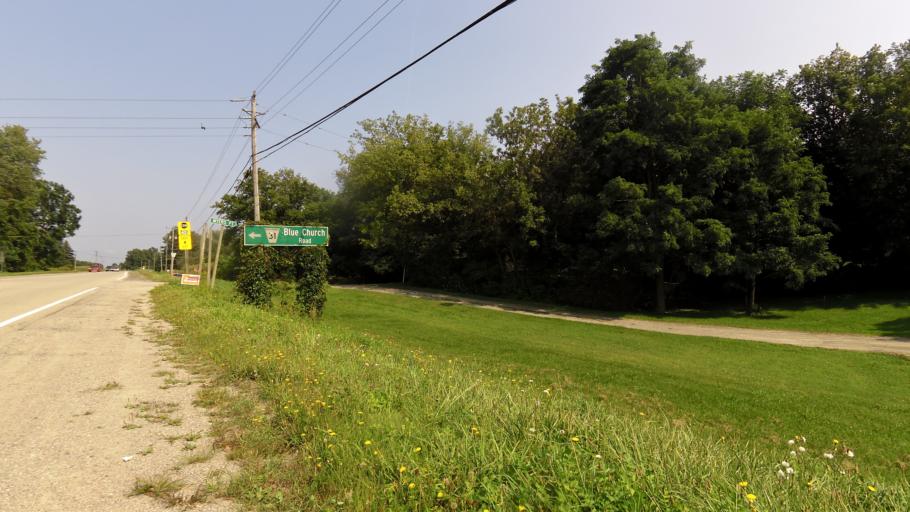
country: CA
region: Ontario
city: Prescott
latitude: 44.6797
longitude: -75.5602
